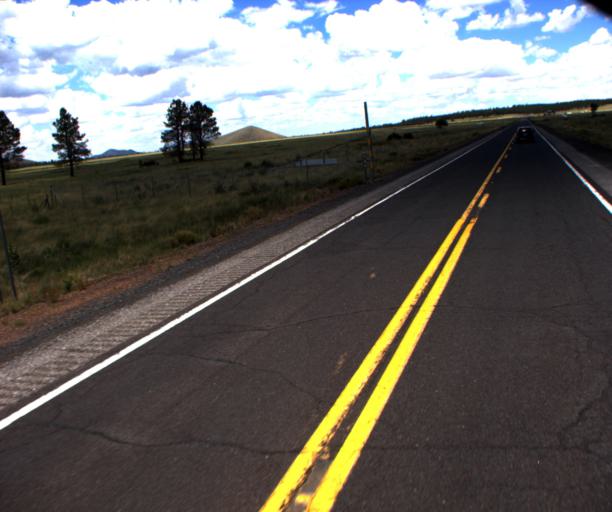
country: US
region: Arizona
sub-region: Coconino County
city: Flagstaff
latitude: 35.4034
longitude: -111.7555
